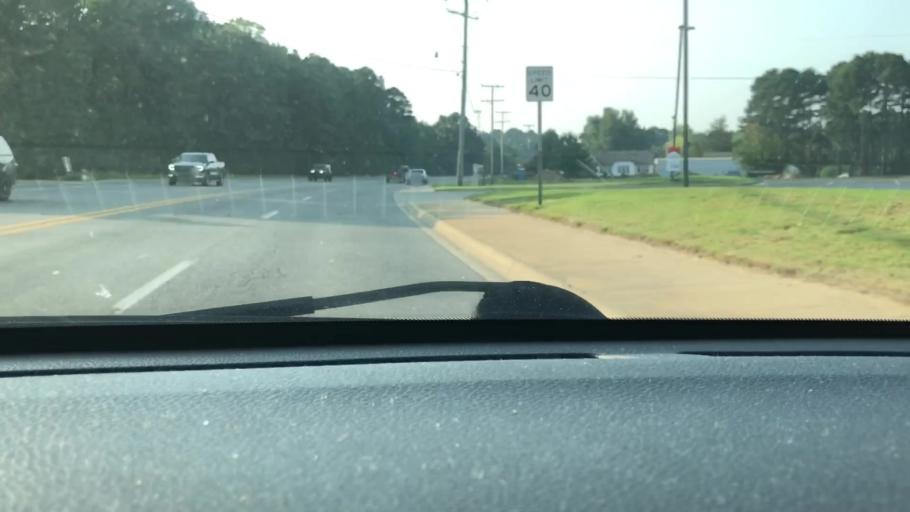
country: US
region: Arkansas
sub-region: Saline County
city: Bryant
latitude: 34.6095
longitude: -92.4932
